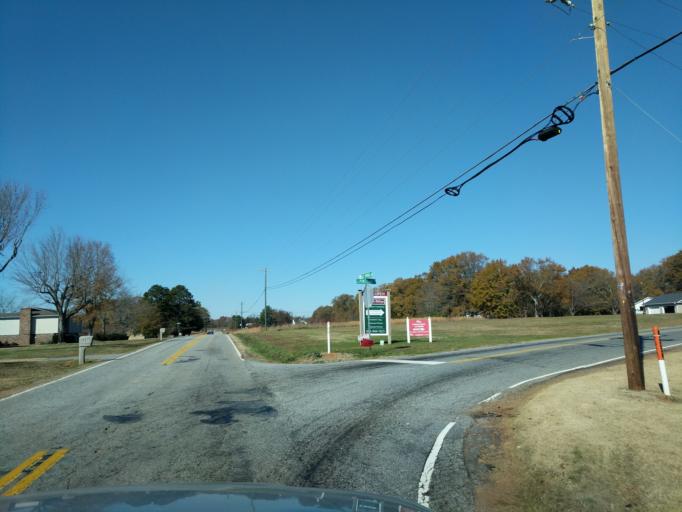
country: US
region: South Carolina
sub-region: Spartanburg County
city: Lyman
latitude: 34.9669
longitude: -82.1430
